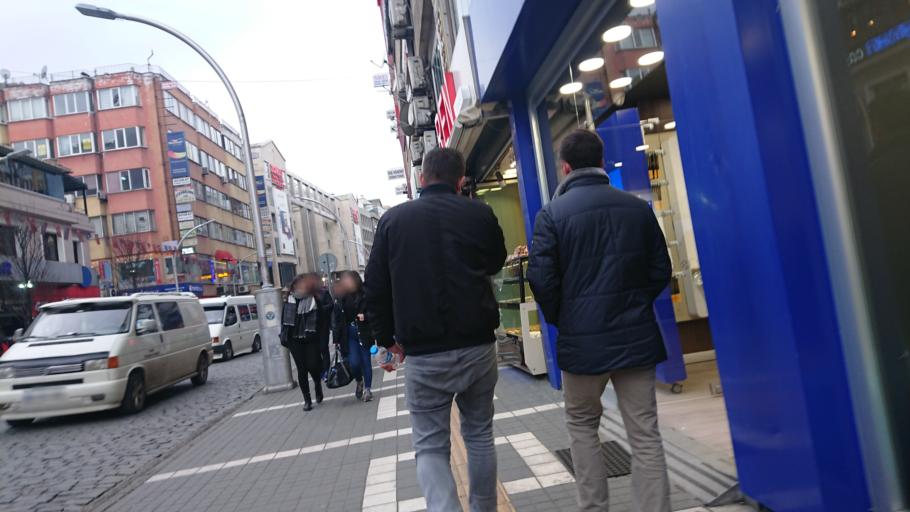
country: TR
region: Trabzon
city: Trabzon
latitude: 41.0056
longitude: 39.7299
